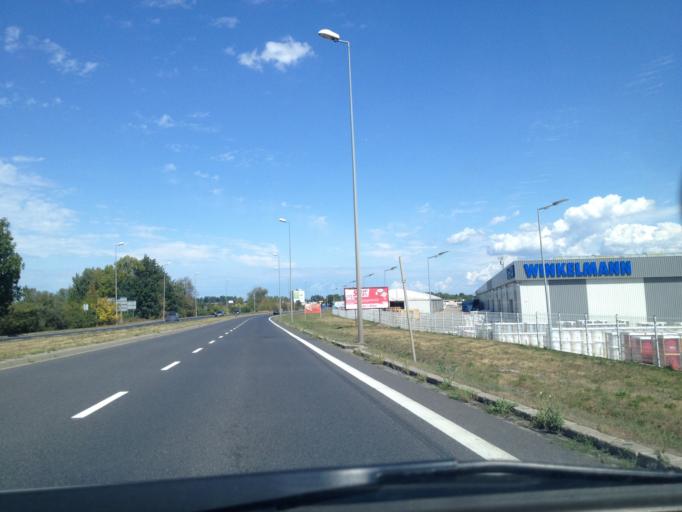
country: PL
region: Lower Silesian Voivodeship
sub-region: Legnica
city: Legnica
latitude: 51.1641
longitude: 16.1730
